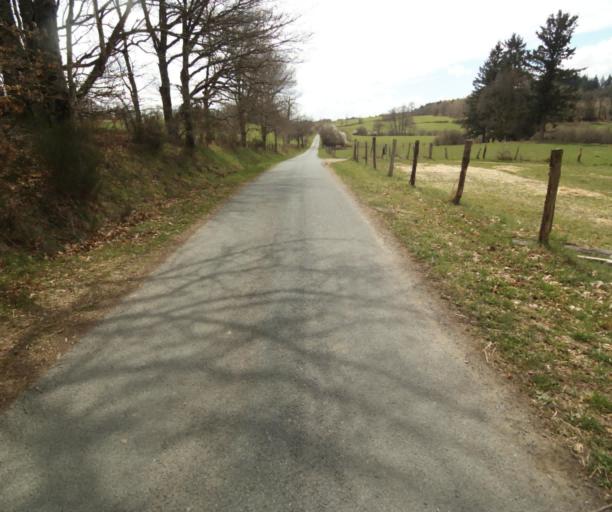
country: FR
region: Limousin
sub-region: Departement de la Correze
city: Correze
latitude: 45.3822
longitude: 1.9623
